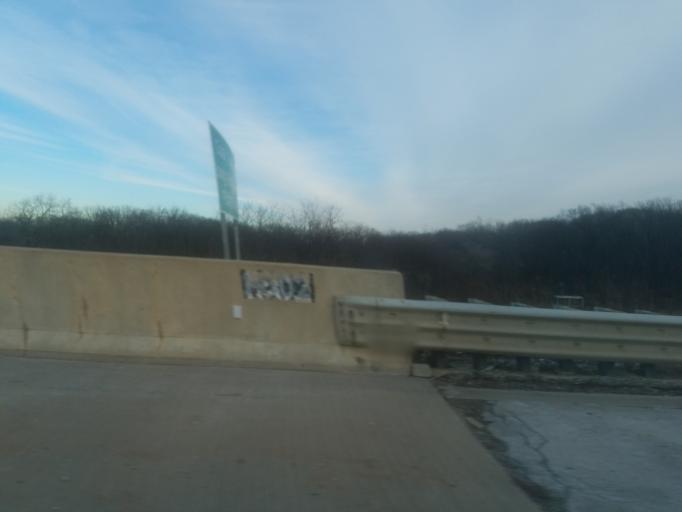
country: US
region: Illinois
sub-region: Cook County
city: Lemont
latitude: 41.6406
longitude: -88.0124
